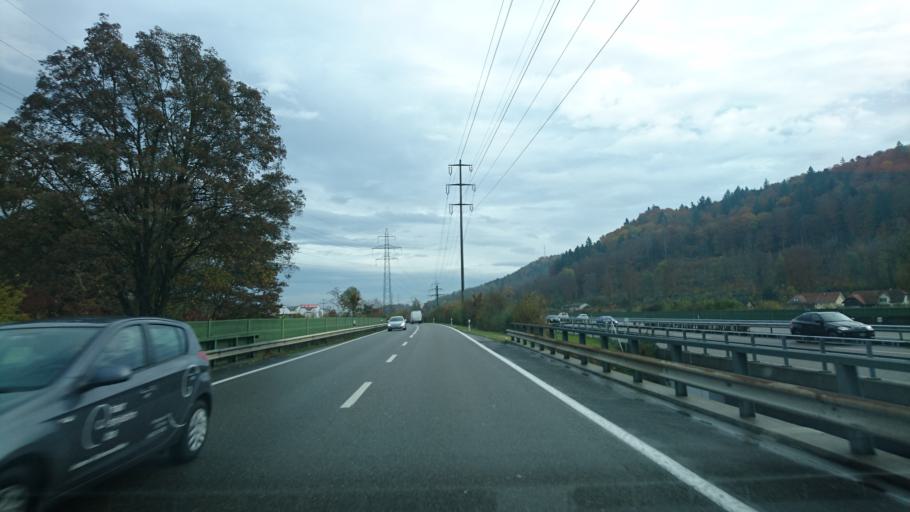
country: CH
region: Aargau
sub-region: Bezirk Aarau
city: Oberentfelden
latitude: 47.3526
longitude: 8.0564
